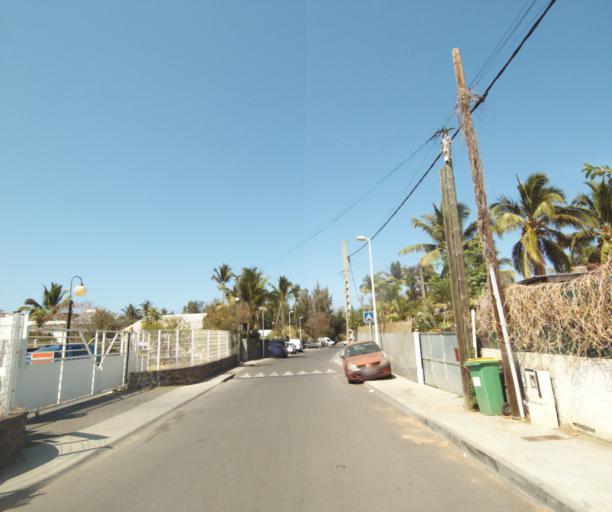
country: RE
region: Reunion
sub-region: Reunion
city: Trois-Bassins
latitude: -21.0983
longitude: 55.2433
